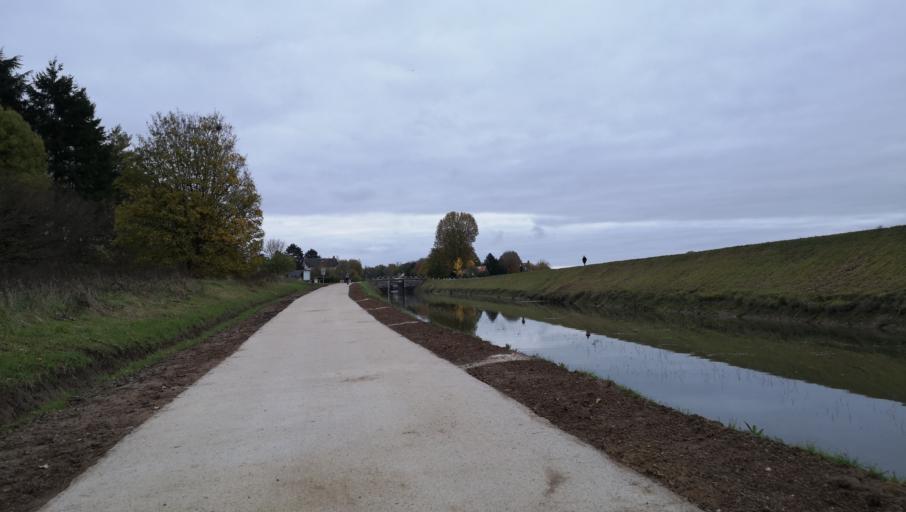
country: FR
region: Centre
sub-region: Departement du Loiret
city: Saint-Jean-de-Braye
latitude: 47.9019
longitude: 1.9809
